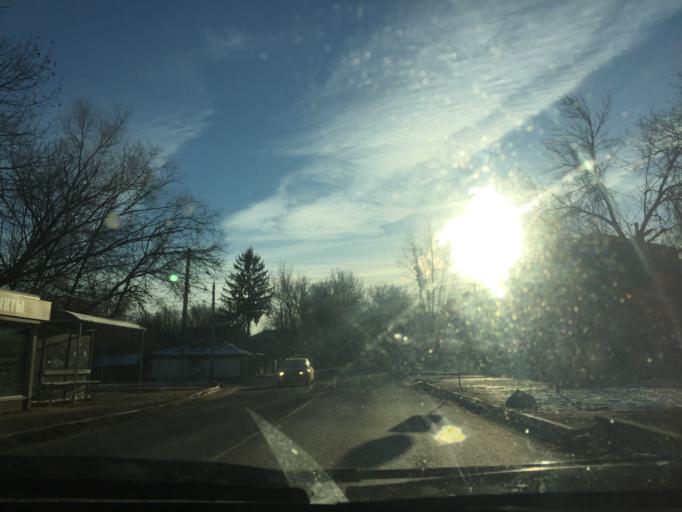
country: RU
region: Tula
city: Tula
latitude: 54.2099
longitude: 37.5959
